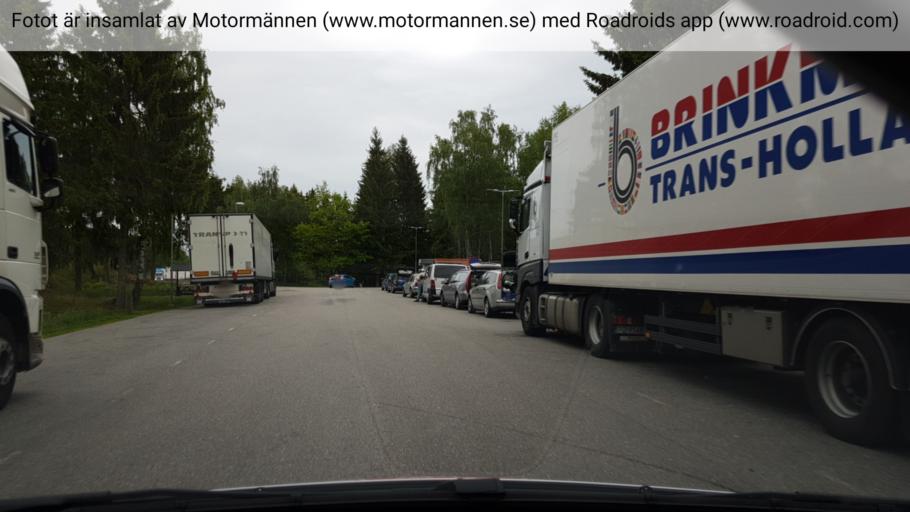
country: SE
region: Vaestmanland
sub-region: Vasteras
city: Skultuna
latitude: 59.5887
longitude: 16.4004
